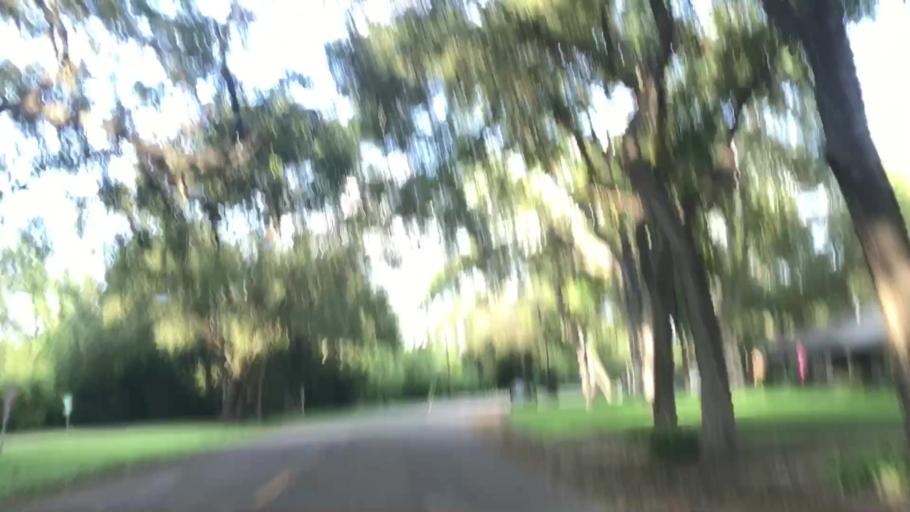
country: US
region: Texas
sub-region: Dallas County
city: Dallas
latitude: 32.7649
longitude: -96.8399
